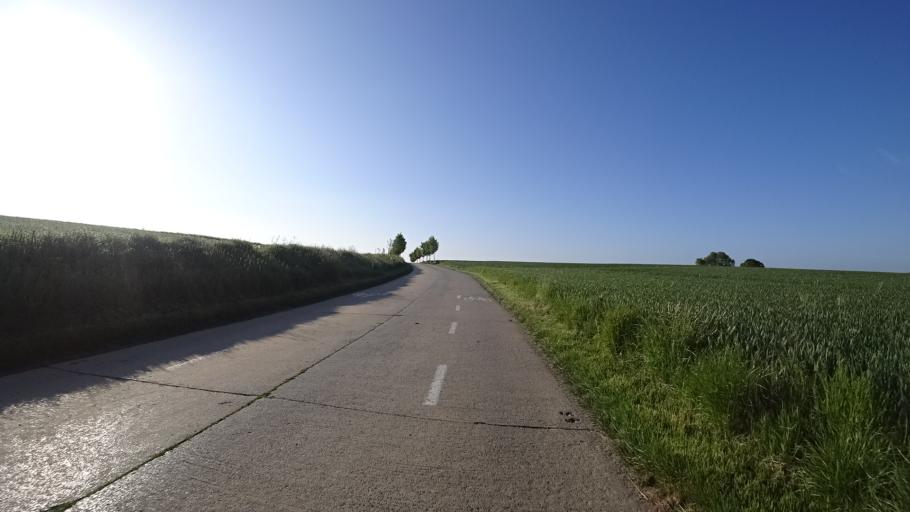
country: BE
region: Wallonia
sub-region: Province du Brabant Wallon
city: Walhain-Saint-Paul
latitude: 50.6360
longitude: 4.6778
